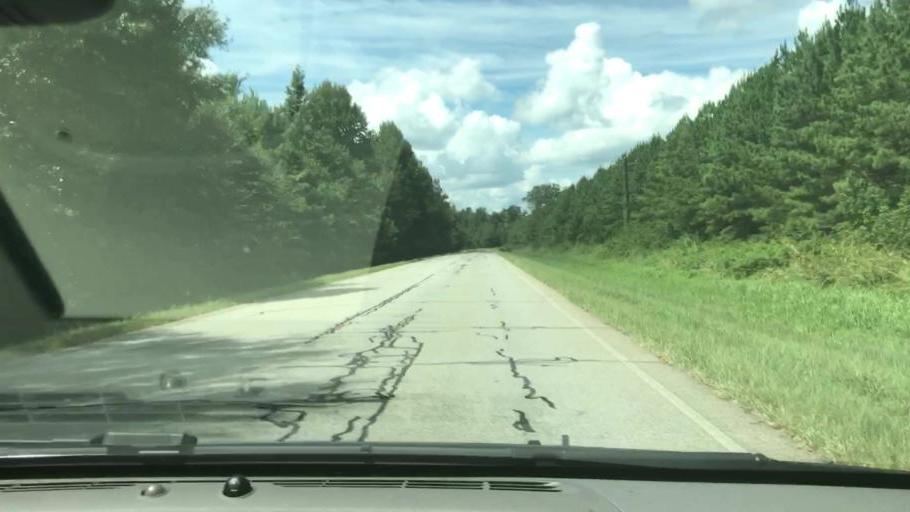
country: US
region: Georgia
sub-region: Stewart County
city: Lumpkin
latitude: 32.1445
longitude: -84.8846
